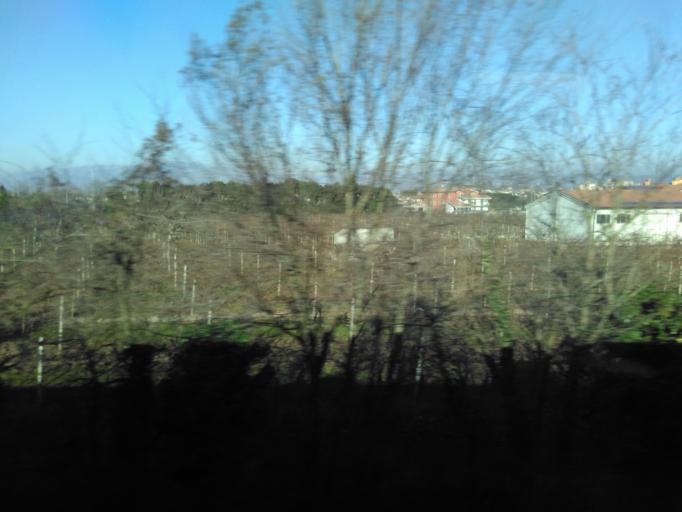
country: IT
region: Veneto
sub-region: Provincia di Verona
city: Dossobuono
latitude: 45.4272
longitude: 10.9376
